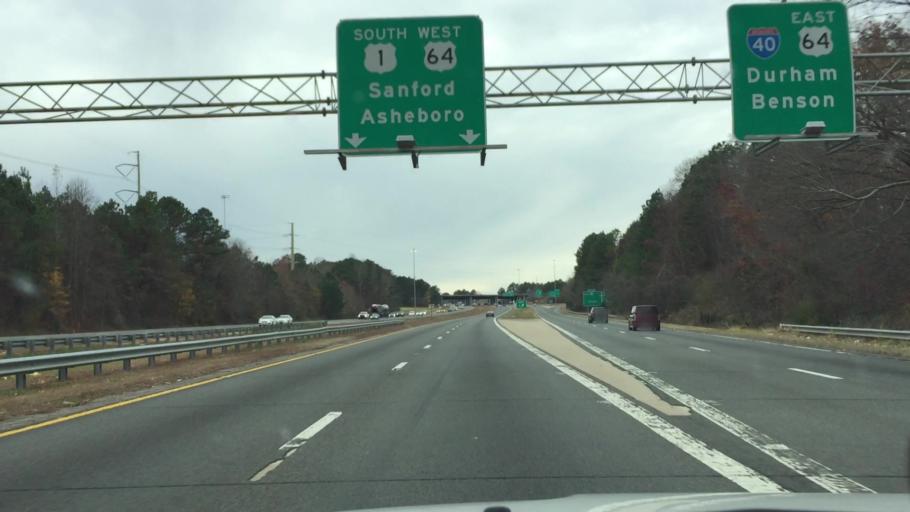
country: US
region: North Carolina
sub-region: Wake County
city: Cary
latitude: 35.7695
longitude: -78.7263
